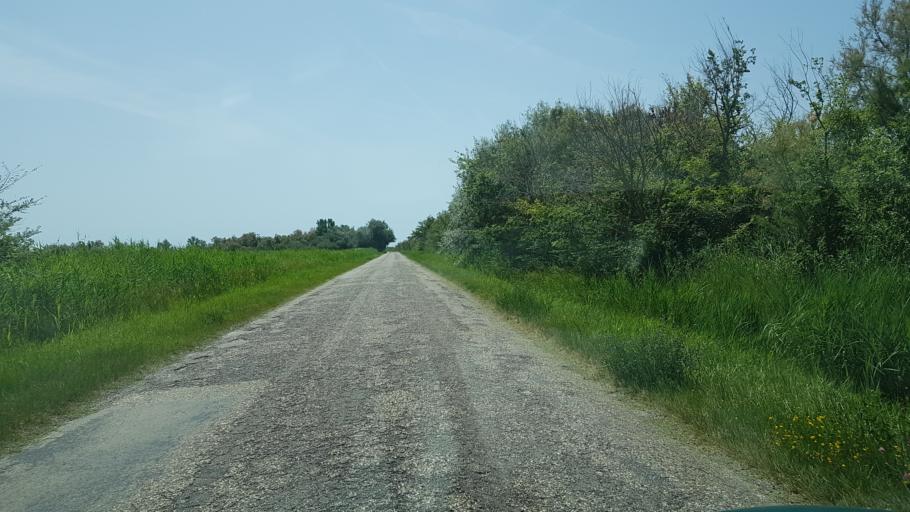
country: FR
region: Provence-Alpes-Cote d'Azur
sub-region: Departement des Bouches-du-Rhone
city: Arles
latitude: 43.5579
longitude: 4.6246
